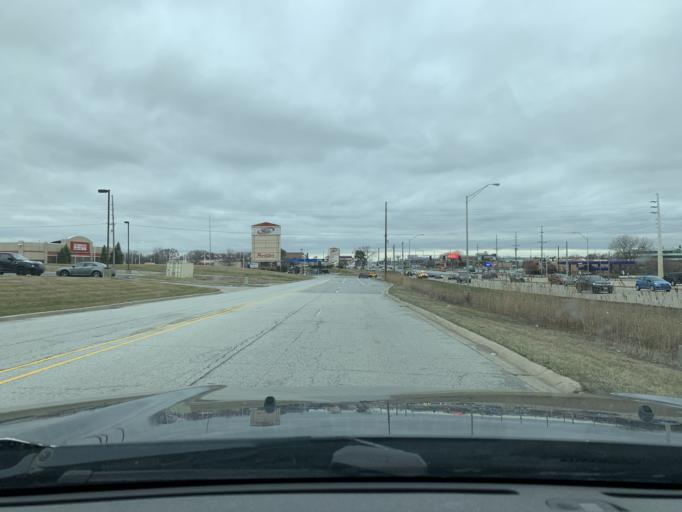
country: US
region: Indiana
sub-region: Lake County
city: Merrillville
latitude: 41.4708
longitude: -87.3295
